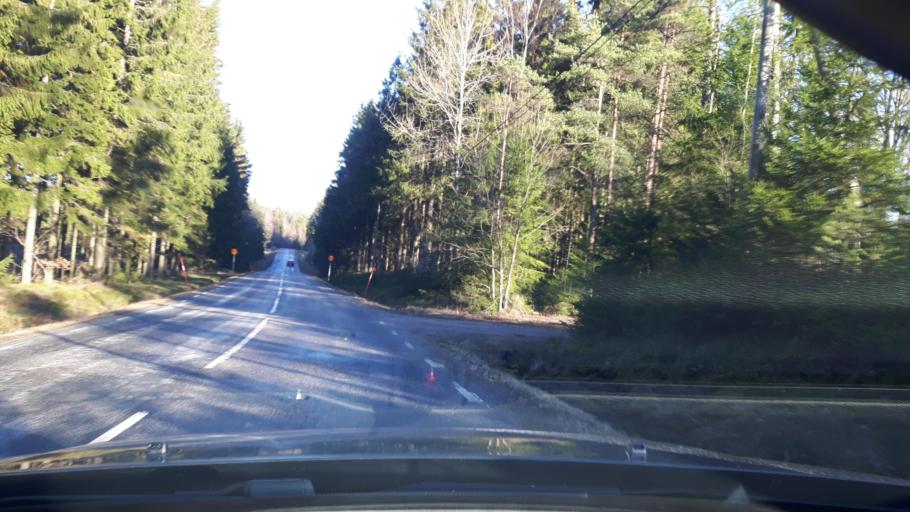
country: SE
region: Vaestra Goetaland
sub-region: Munkedals Kommun
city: Munkedal
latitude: 58.5204
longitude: 11.6846
